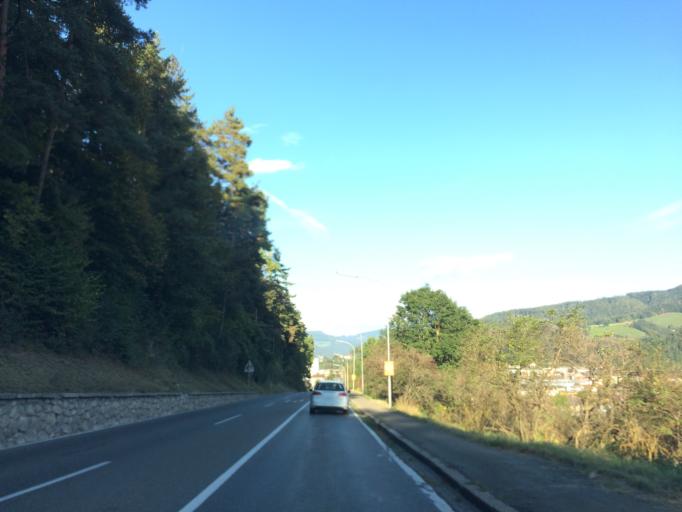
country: AT
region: Styria
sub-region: Politischer Bezirk Leoben
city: Leoben
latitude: 47.3669
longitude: 15.0780
